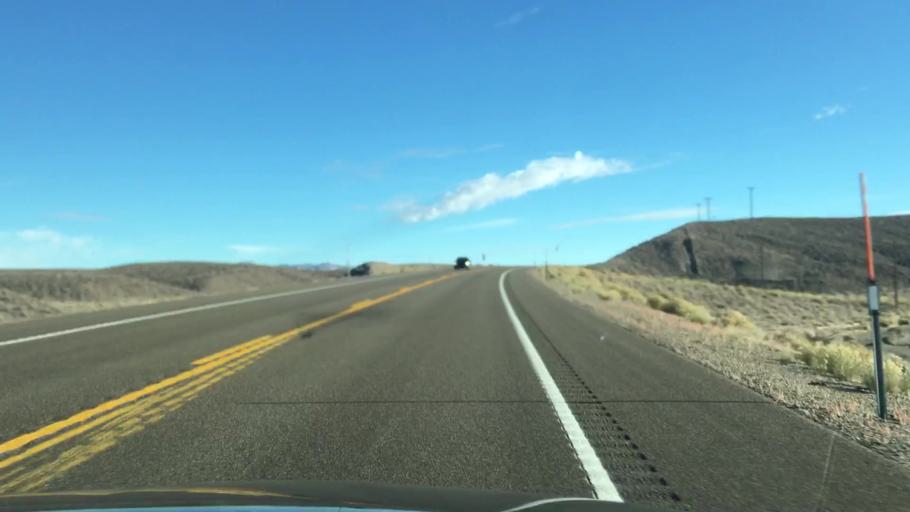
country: US
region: Nevada
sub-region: Mineral County
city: Hawthorne
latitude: 38.2192
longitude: -118.0080
